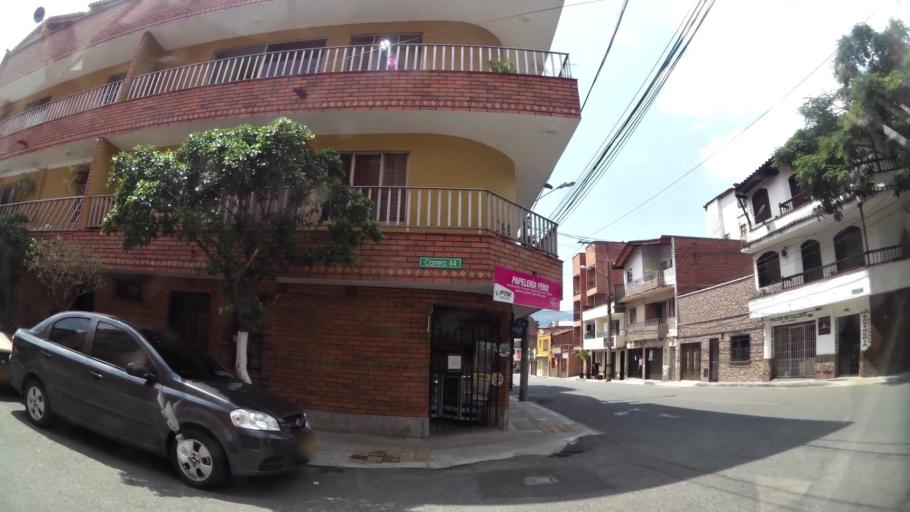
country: CO
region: Antioquia
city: Envigado
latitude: 6.1736
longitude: -75.5874
